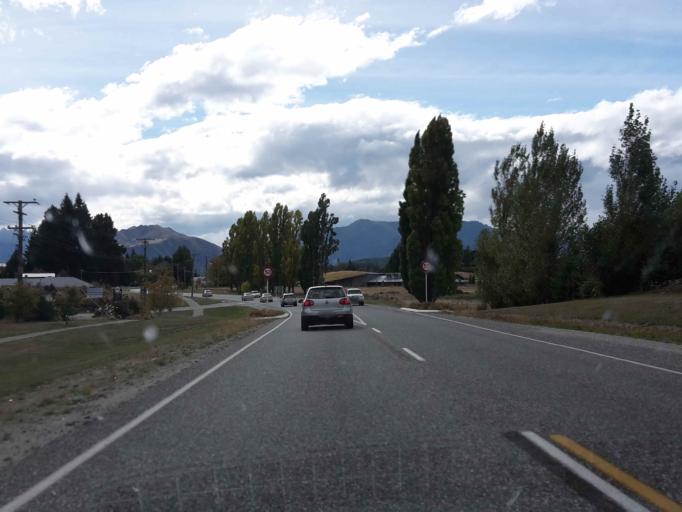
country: NZ
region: Otago
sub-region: Queenstown-Lakes District
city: Wanaka
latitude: -44.7127
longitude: 169.1370
